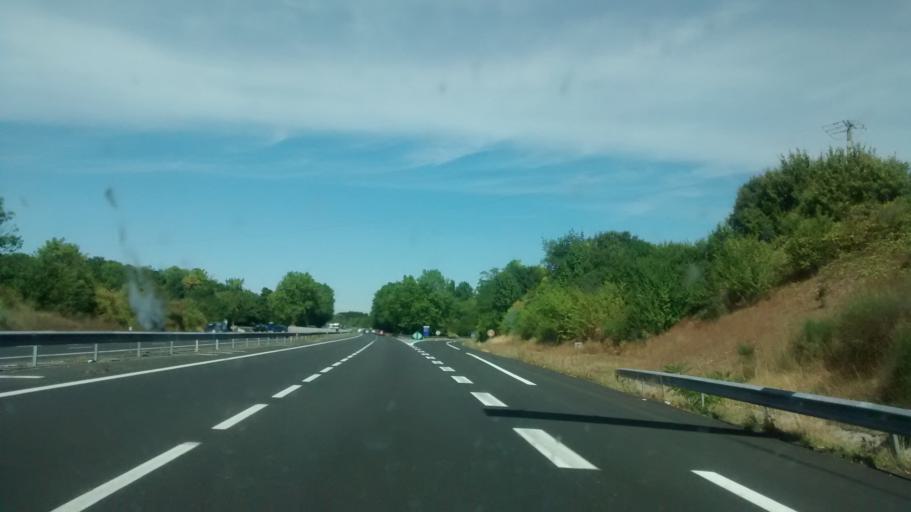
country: FR
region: Poitou-Charentes
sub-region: Departement de la Charente-Maritime
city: Chermignac
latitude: 45.7010
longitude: -0.6505
